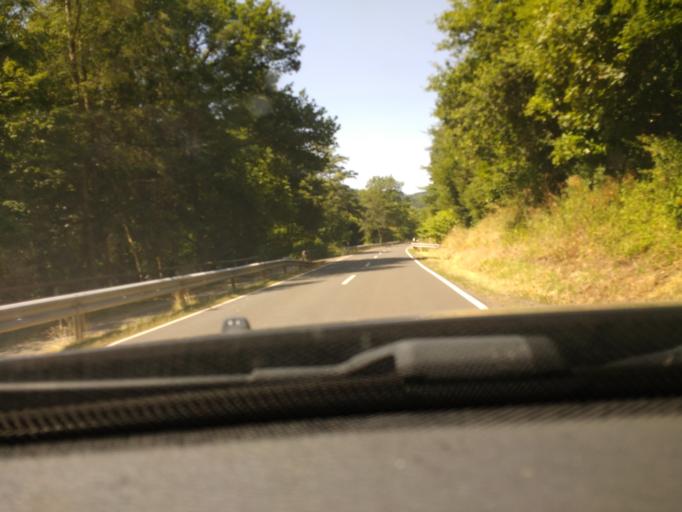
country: DE
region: Rheinland-Pfalz
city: Plein
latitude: 50.0119
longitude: 6.8764
